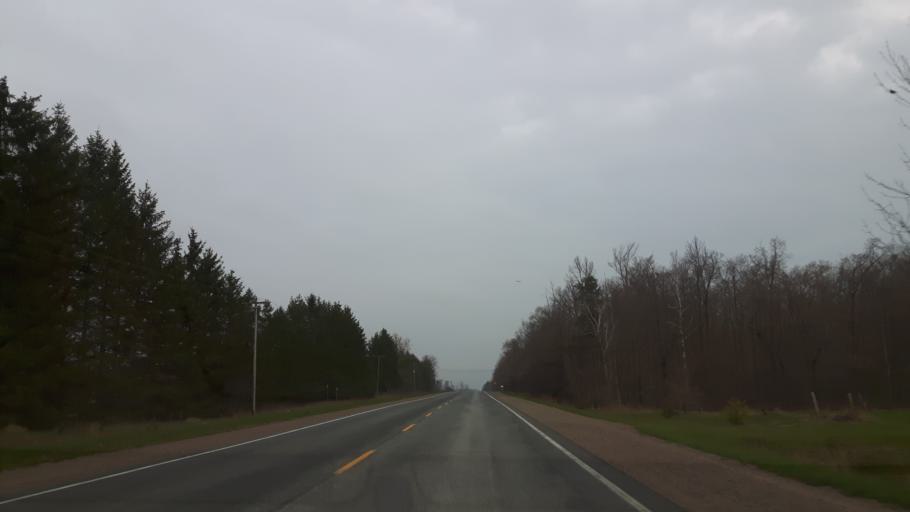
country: CA
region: Ontario
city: Bluewater
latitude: 43.5425
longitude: -81.6907
